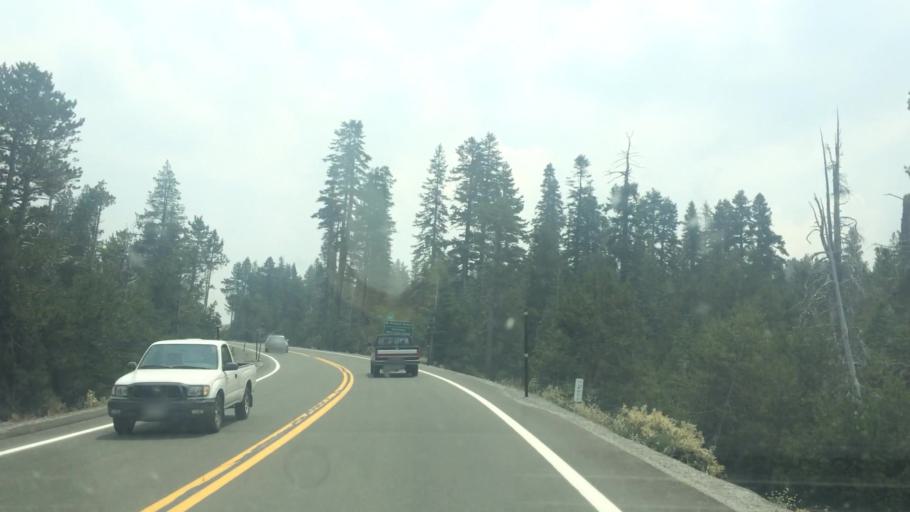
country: US
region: California
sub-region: El Dorado County
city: South Lake Tahoe
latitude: 38.6533
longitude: -120.1344
